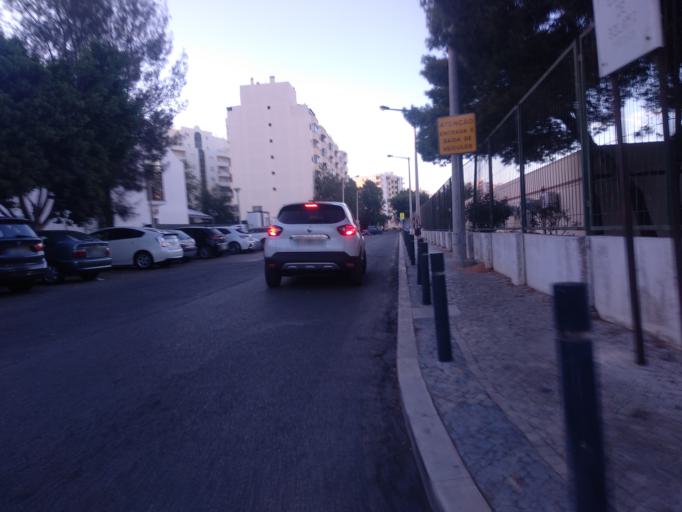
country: PT
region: Faro
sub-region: Faro
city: Faro
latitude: 37.0238
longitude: -7.9299
